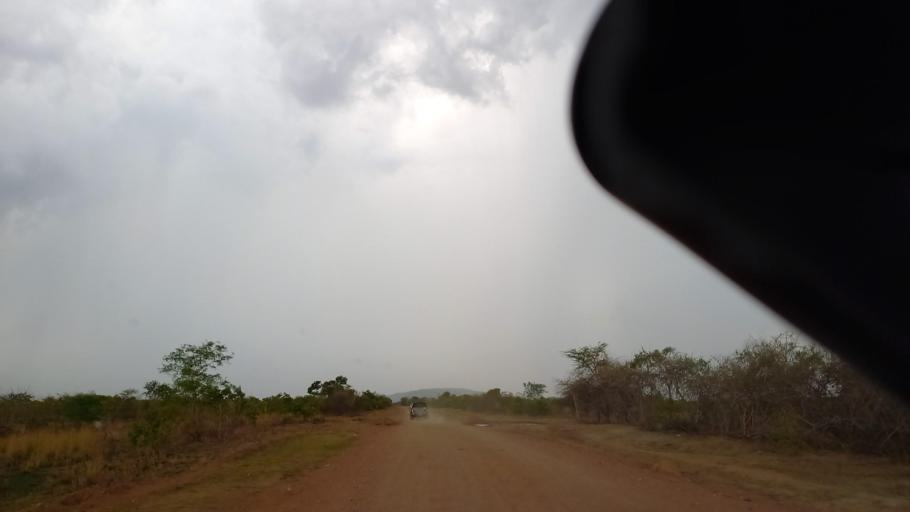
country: ZM
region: Lusaka
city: Kafue
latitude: -15.8689
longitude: 28.1959
